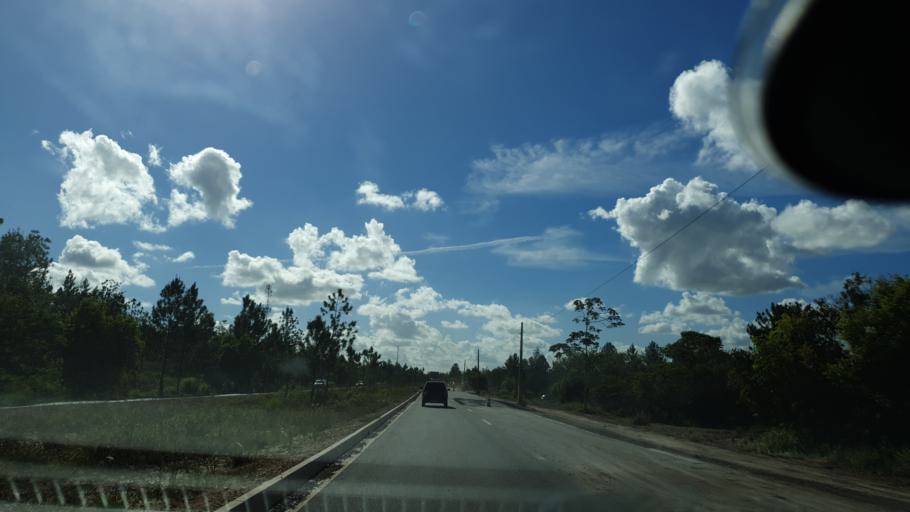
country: BR
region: Bahia
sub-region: Camacari
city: Camacari
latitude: -12.6825
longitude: -38.2946
